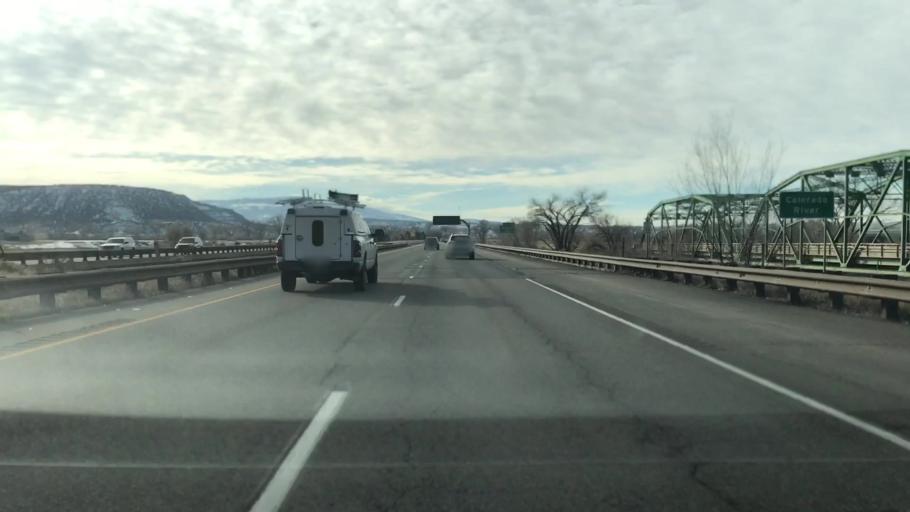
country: US
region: Colorado
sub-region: Garfield County
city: Parachute
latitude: 39.3393
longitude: -108.1930
